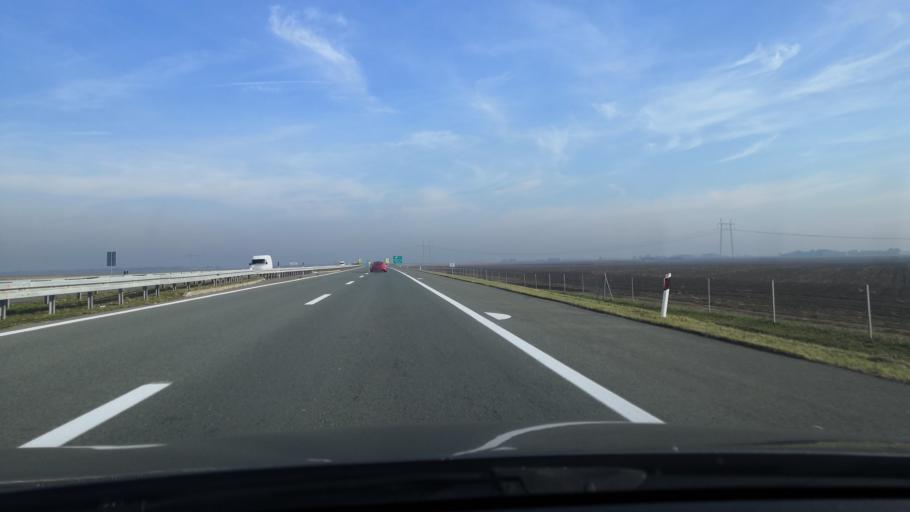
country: RS
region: Autonomna Pokrajina Vojvodina
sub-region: Severnobacki Okrug
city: Subotica
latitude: 46.0090
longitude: 19.7286
